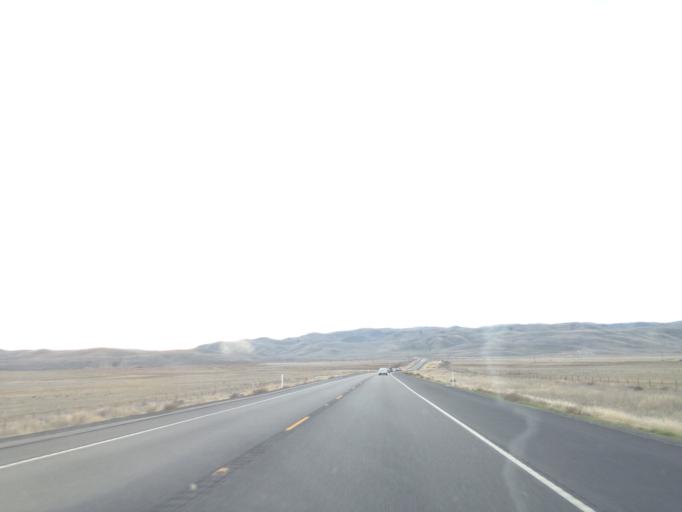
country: US
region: California
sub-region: San Luis Obispo County
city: Shandon
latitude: 35.7374
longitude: -120.2694
